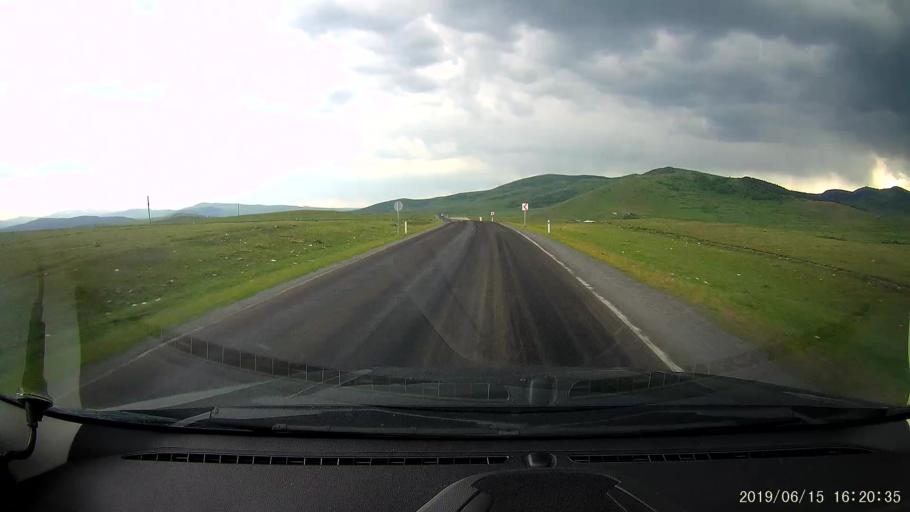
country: TR
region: Ardahan
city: Hanak
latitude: 41.2117
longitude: 42.8469
